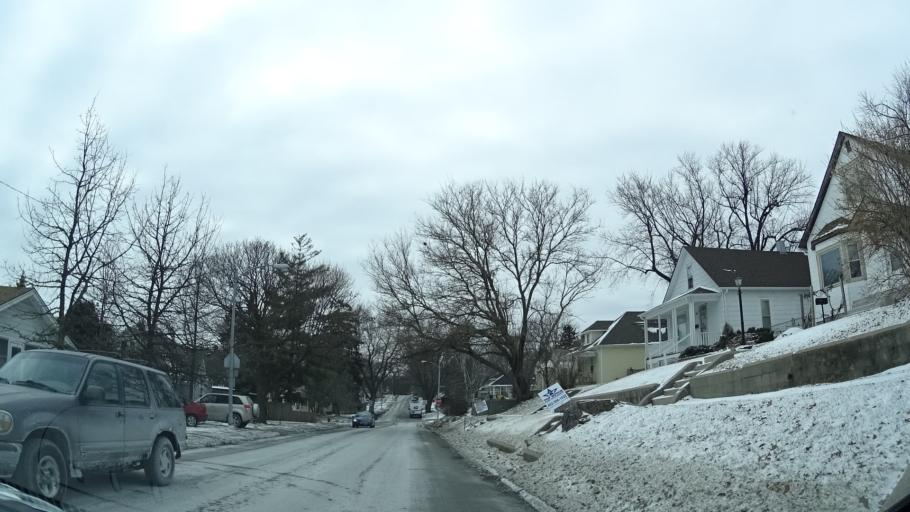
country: US
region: Nebraska
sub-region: Douglas County
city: Omaha
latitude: 41.2821
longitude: -96.0048
